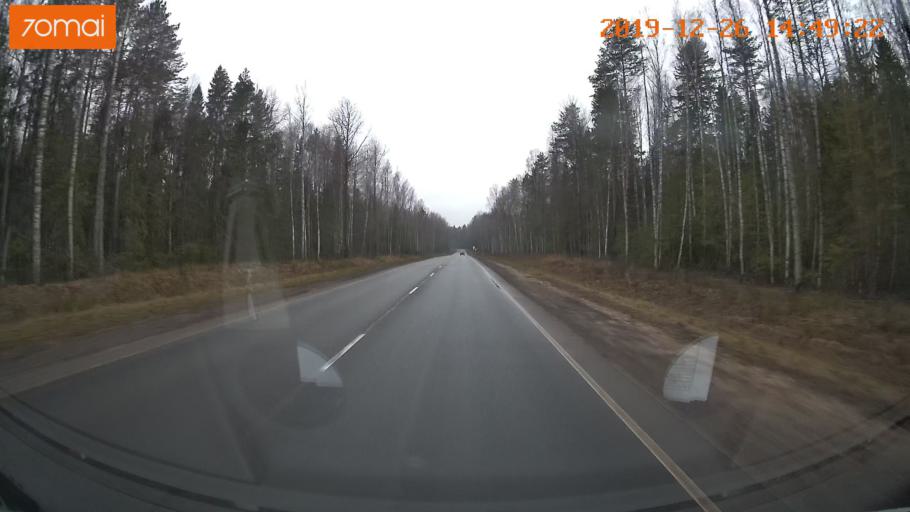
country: RU
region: Jaroslavl
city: Poshekhon'ye
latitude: 58.3394
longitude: 38.9480
